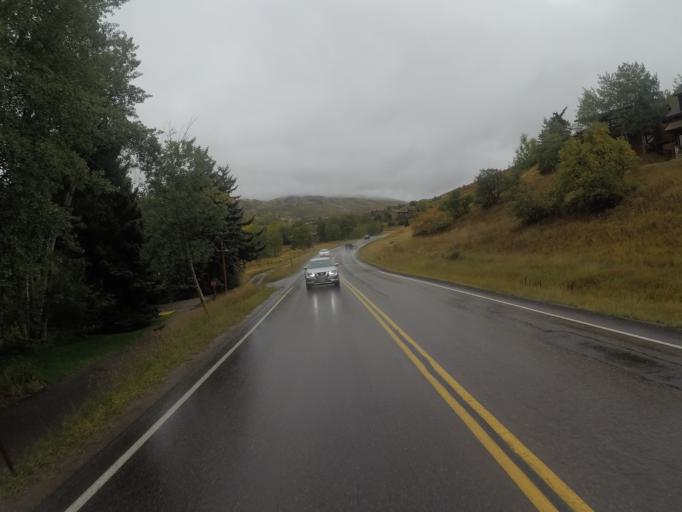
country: US
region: Colorado
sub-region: Pitkin County
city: Snowmass Village
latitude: 39.2164
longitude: -106.9360
